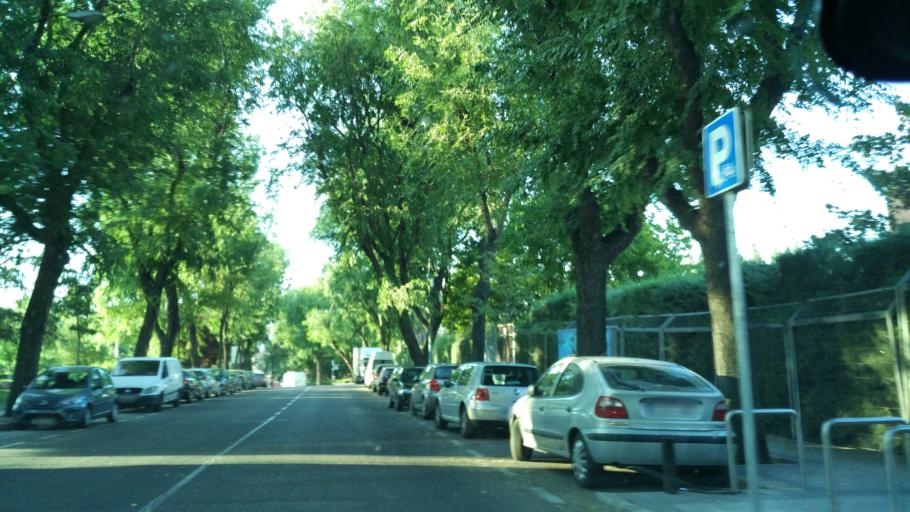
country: ES
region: Madrid
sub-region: Provincia de Madrid
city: Tetuan de las Victorias
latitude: 40.4604
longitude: -3.7123
